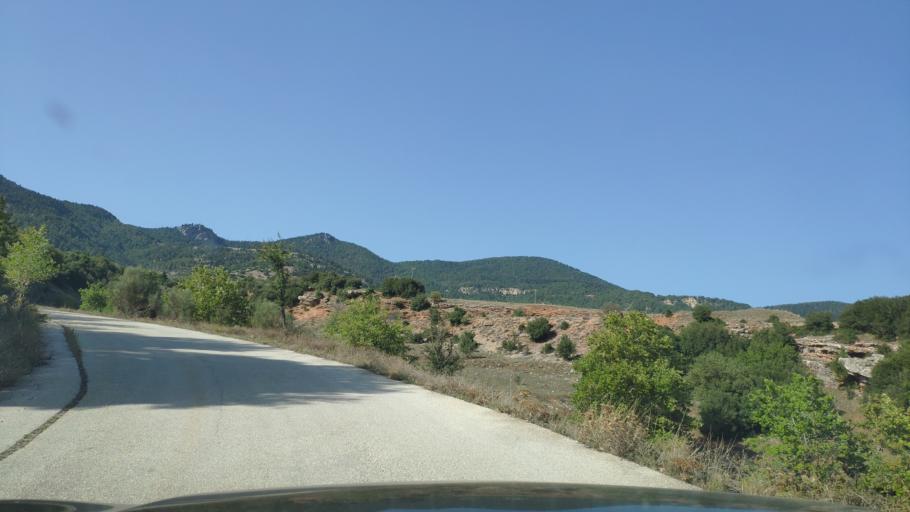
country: GR
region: West Greece
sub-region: Nomos Achaias
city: Aiyira
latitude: 37.9857
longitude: 22.3589
